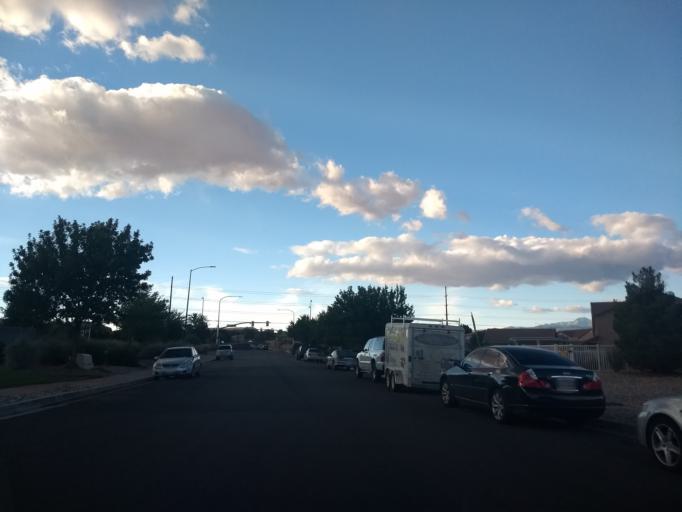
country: US
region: Utah
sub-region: Washington County
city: Washington
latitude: 37.1032
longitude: -113.5295
